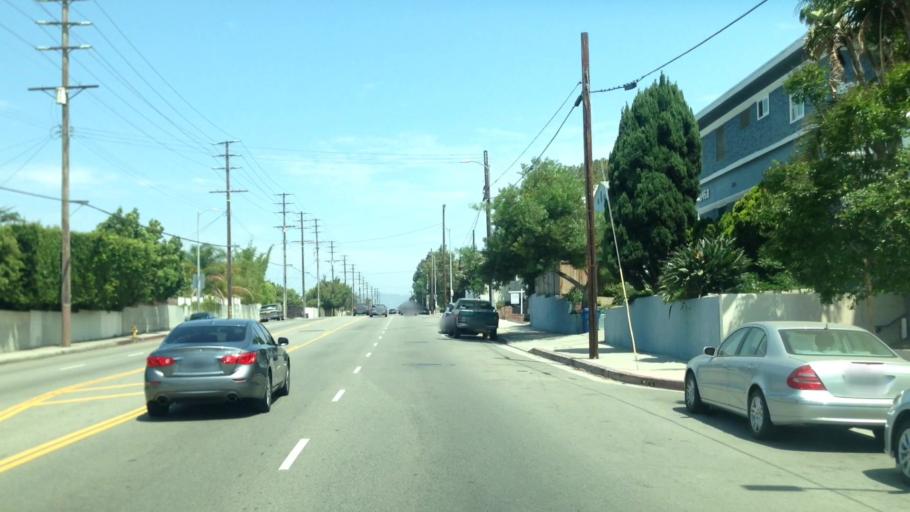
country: US
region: California
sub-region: Los Angeles County
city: Marina del Rey
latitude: 34.0111
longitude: -118.4391
